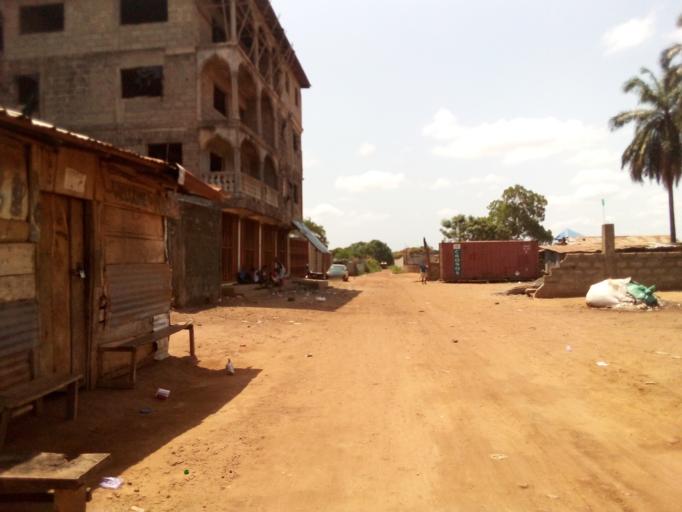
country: SL
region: Western Area
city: Waterloo
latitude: 8.3359
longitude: -13.0303
